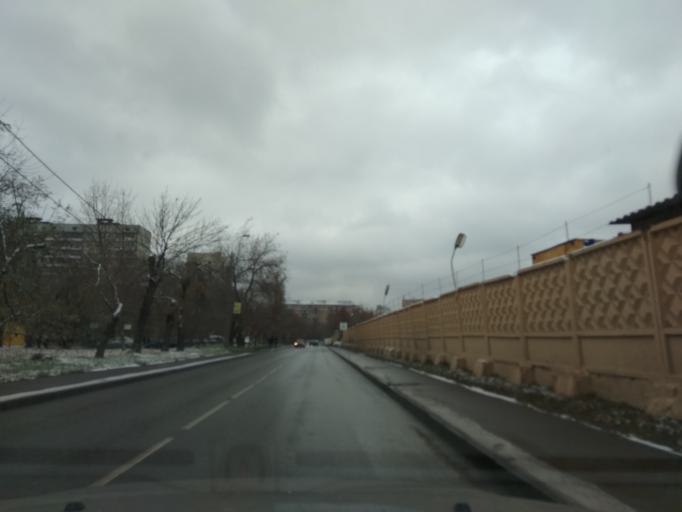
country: RU
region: Moskovskaya
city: Khoroshevo-Mnevniki
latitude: 55.7947
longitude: 37.4660
